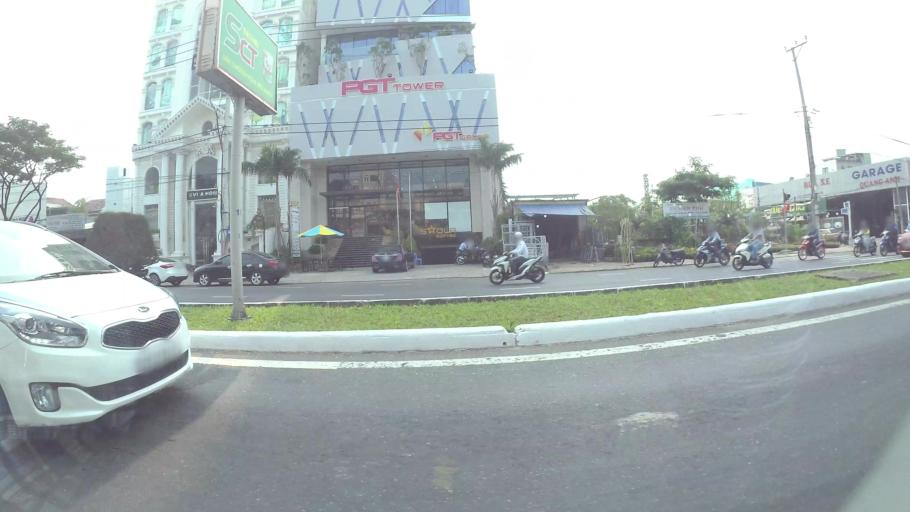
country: VN
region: Da Nang
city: Cam Le
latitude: 16.0418
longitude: 108.2104
